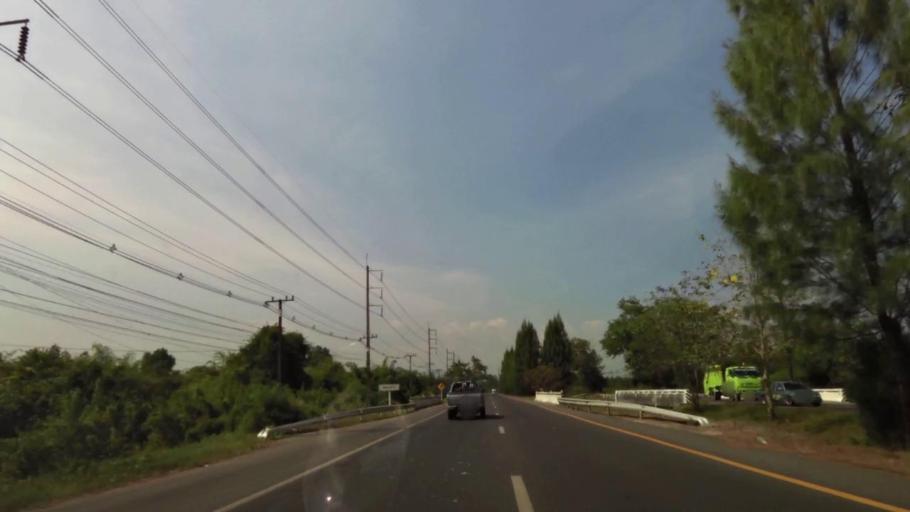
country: TH
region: Chanthaburi
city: Chanthaburi
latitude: 12.6402
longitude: 102.1336
